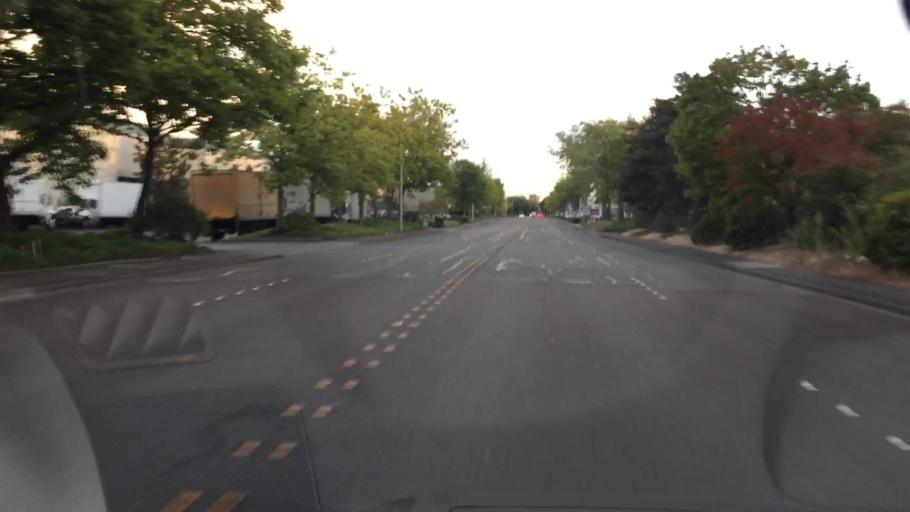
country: US
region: Washington
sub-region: King County
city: Tukwila
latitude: 47.4467
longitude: -122.2545
